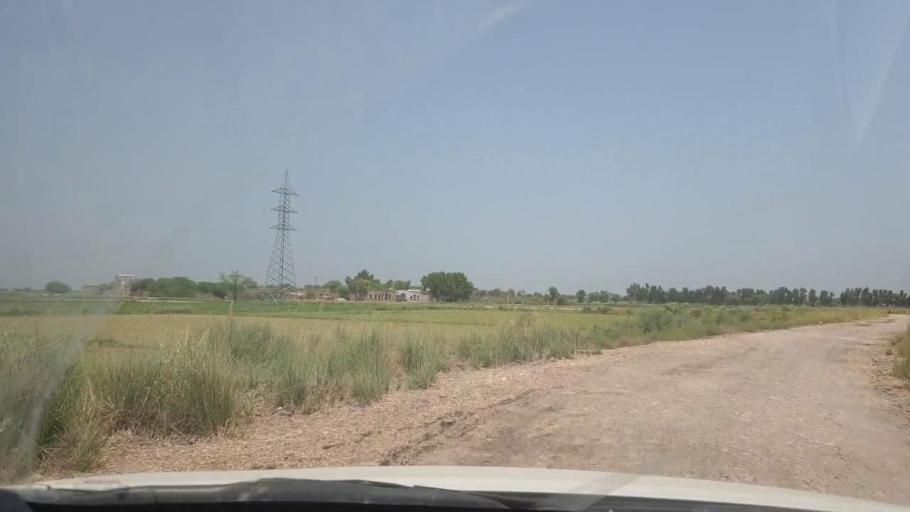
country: PK
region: Sindh
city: Lakhi
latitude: 27.8645
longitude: 68.6970
